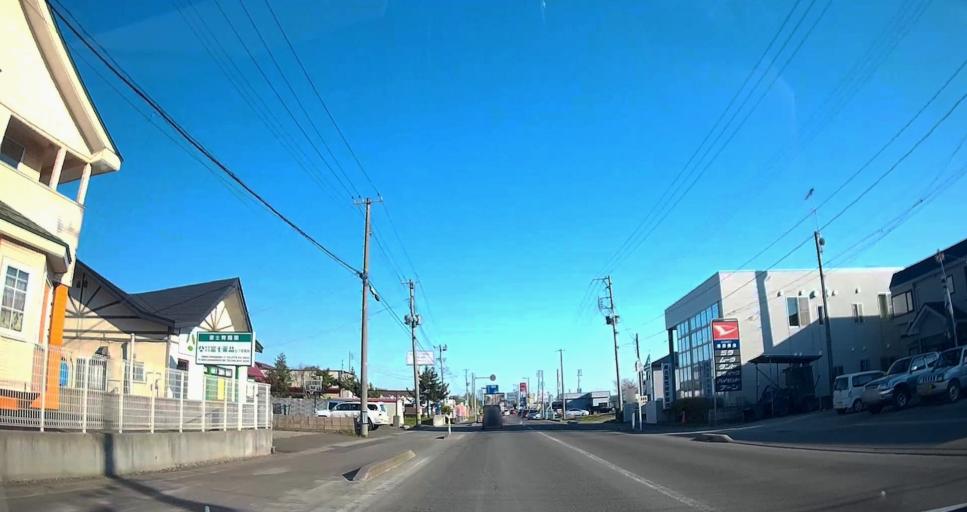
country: JP
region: Aomori
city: Mutsu
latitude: 41.3066
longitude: 141.2193
